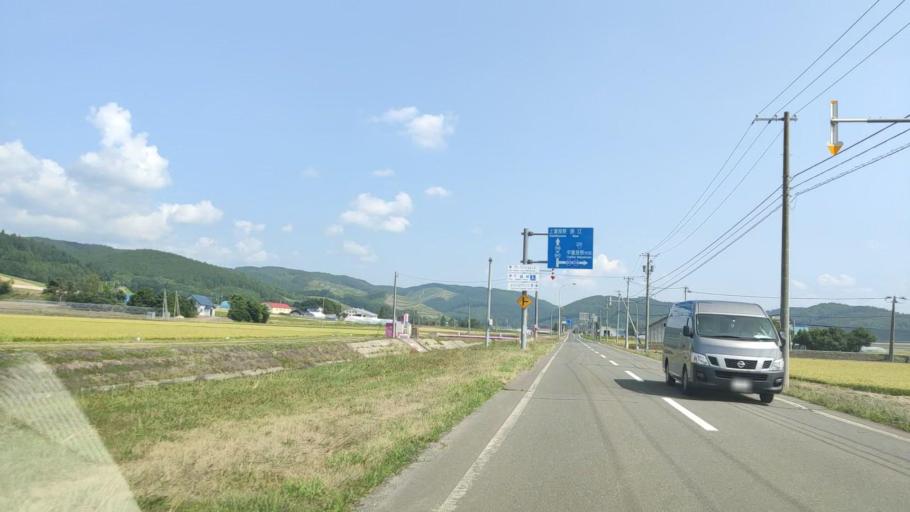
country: JP
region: Hokkaido
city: Shimo-furano
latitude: 43.4023
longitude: 142.3942
